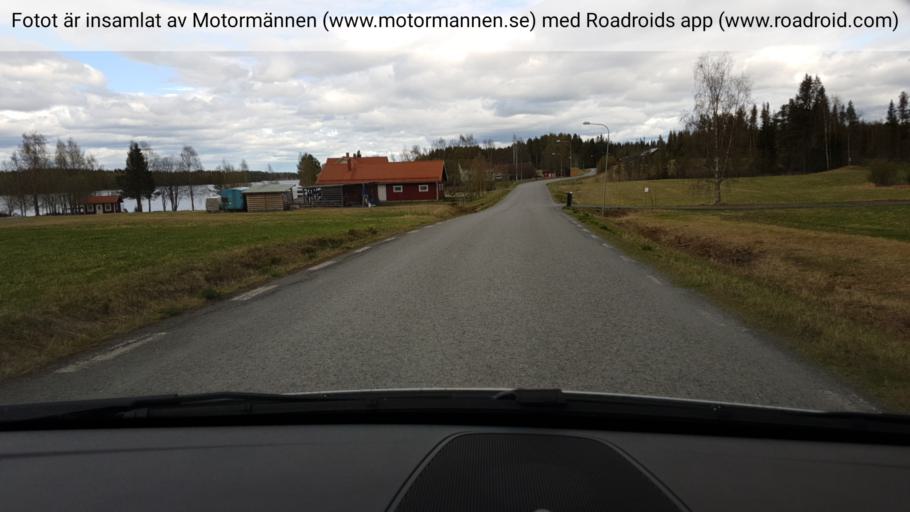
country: SE
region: Jaemtland
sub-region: OEstersunds Kommun
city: Lit
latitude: 63.2961
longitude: 14.9775
